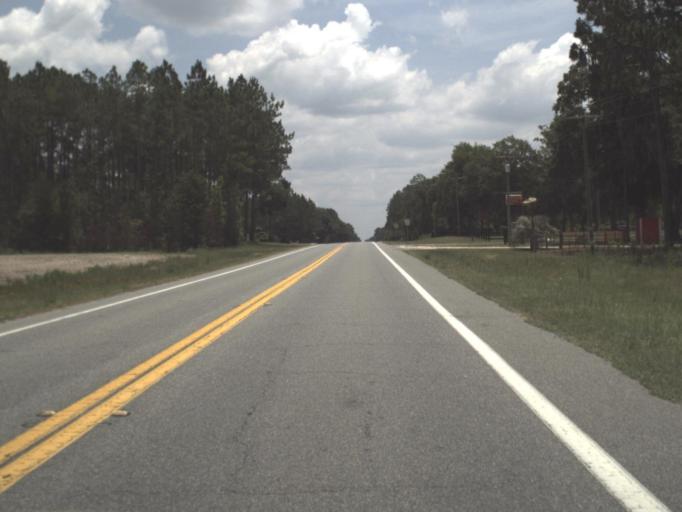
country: US
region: Florida
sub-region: Hamilton County
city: Jasper
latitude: 30.4901
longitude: -83.1291
